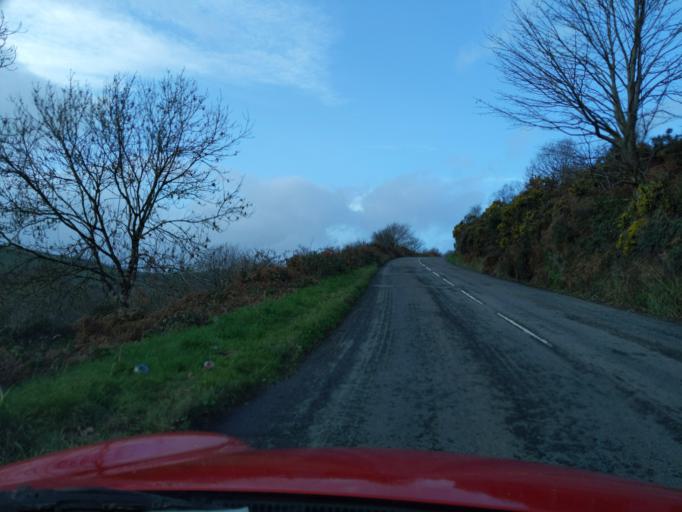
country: GB
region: England
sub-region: Devon
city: Great Torrington
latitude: 50.9506
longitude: -4.1550
